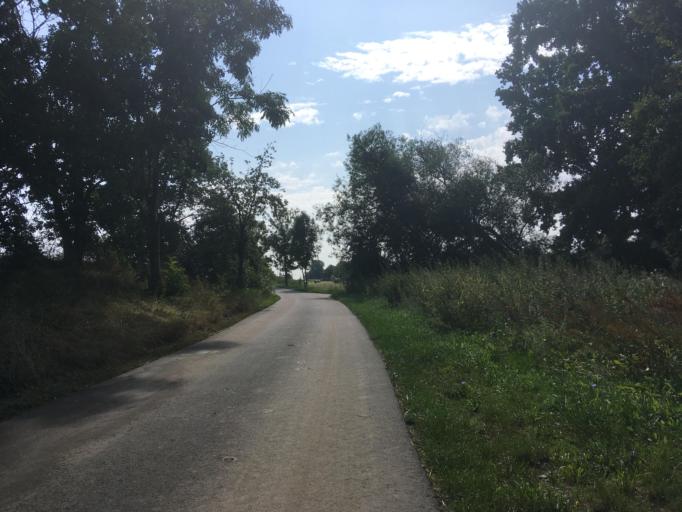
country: DE
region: Saxony
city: Elsnig
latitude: 51.6139
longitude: 12.9277
